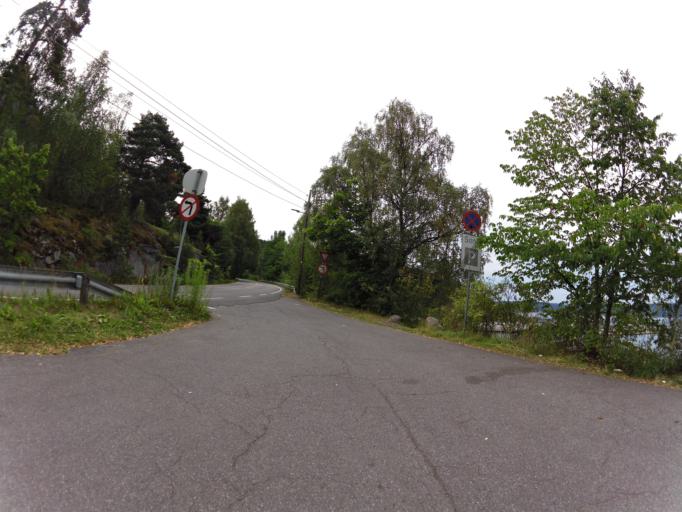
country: NO
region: Akershus
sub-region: Oppegard
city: Kolbotn
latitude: 59.8309
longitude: 10.7674
